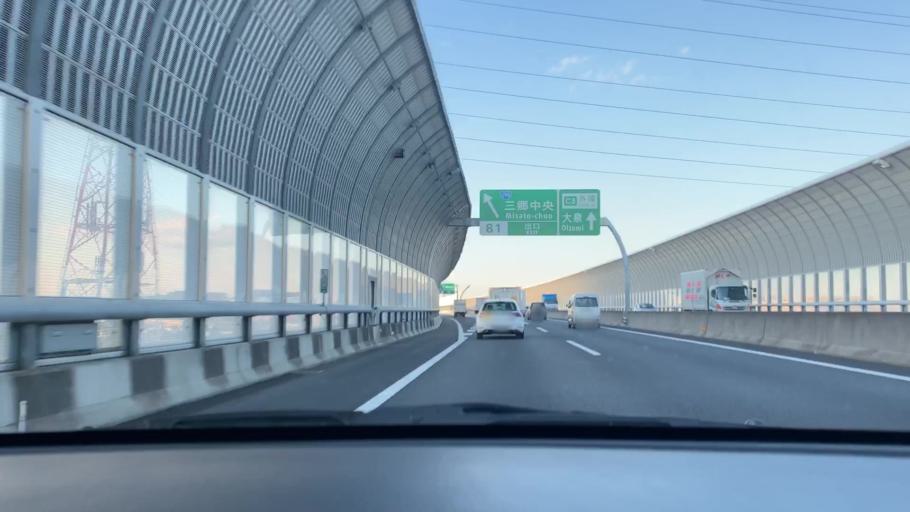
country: JP
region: Saitama
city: Yashio-shi
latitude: 35.8227
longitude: 139.8725
